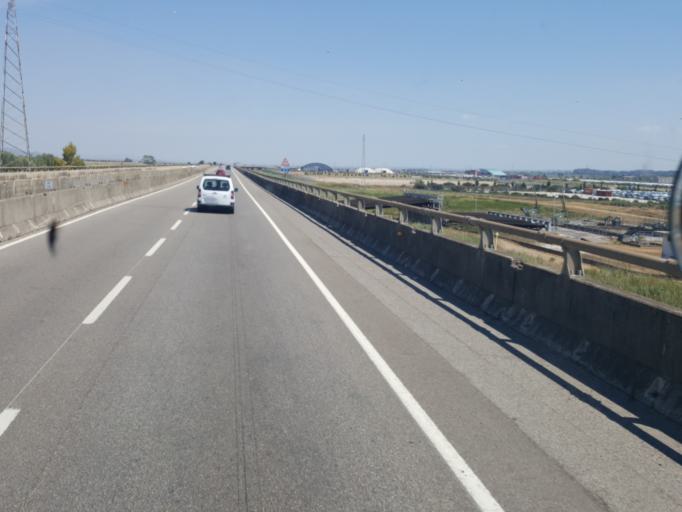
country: IT
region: Tuscany
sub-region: Provincia di Livorno
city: Guasticce
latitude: 43.6055
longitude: 10.3855
